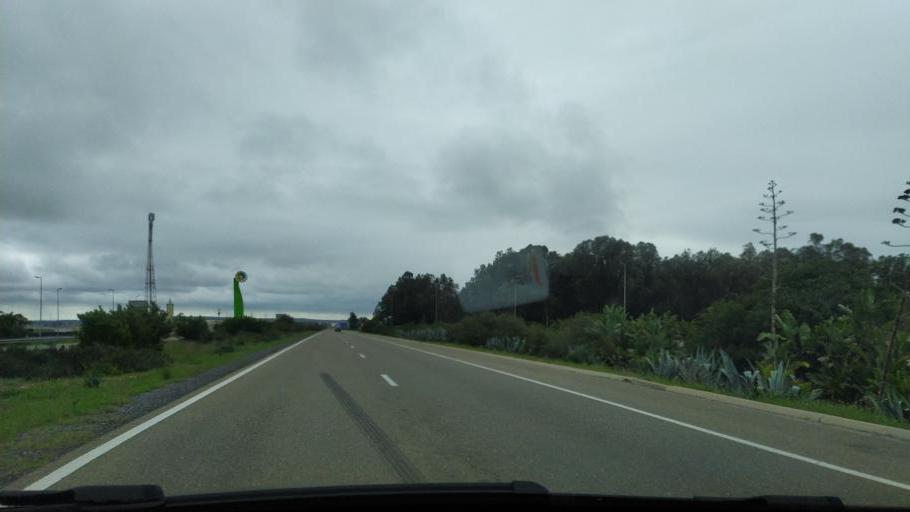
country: MA
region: Gharb-Chrarda-Beni Hssen
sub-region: Kenitra Province
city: Lalla Mimouna
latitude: 34.8761
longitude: -6.2142
